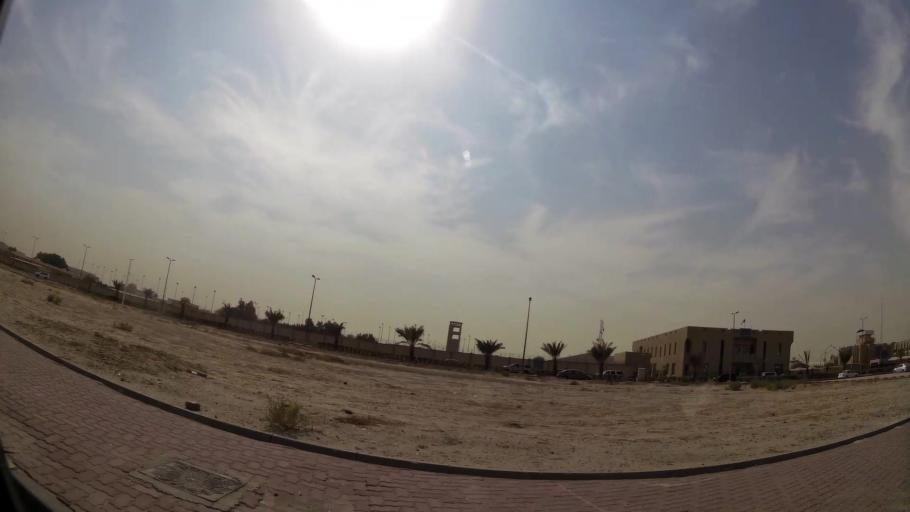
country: KW
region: Al Farwaniyah
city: Janub as Surrah
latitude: 29.2715
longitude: 48.0075
